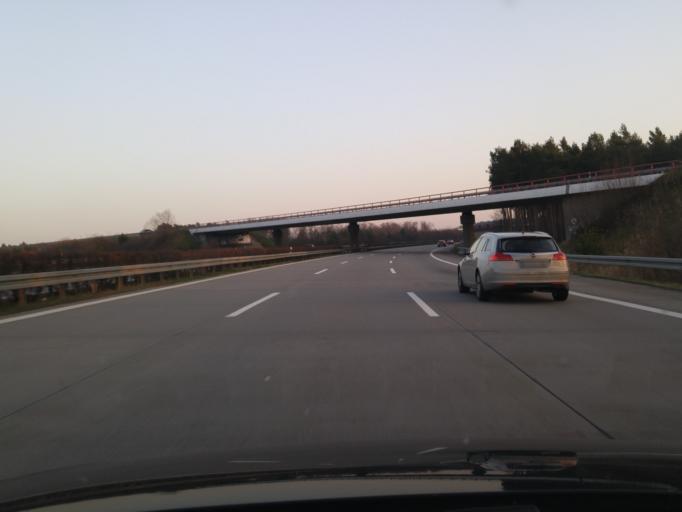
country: DE
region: Brandenburg
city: Gross Kreutz
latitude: 52.3376
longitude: 12.8085
